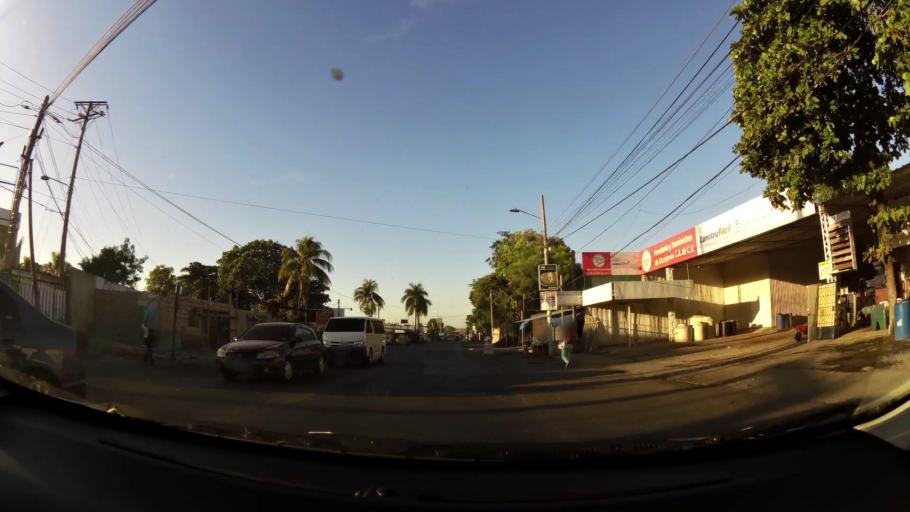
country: SV
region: Sonsonate
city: Sonsonate
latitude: 13.7164
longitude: -89.7237
